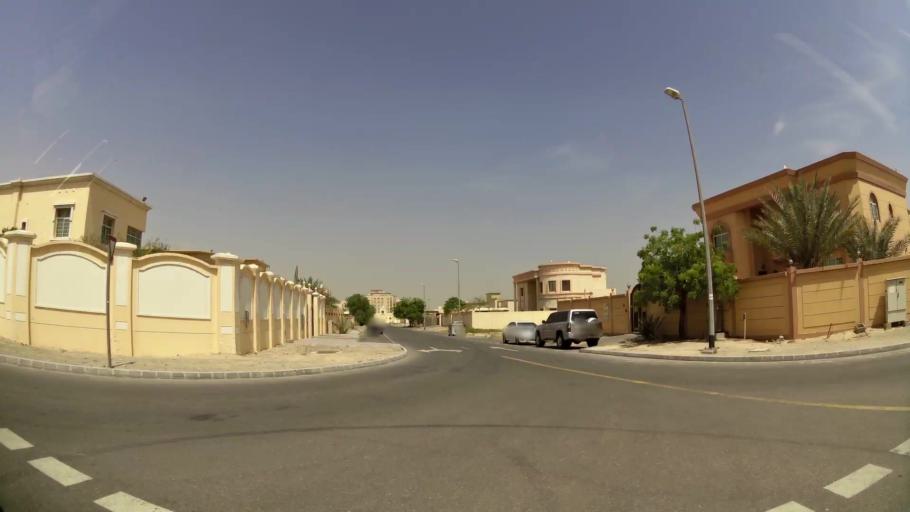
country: AE
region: Ash Shariqah
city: Sharjah
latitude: 25.1867
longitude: 55.4134
